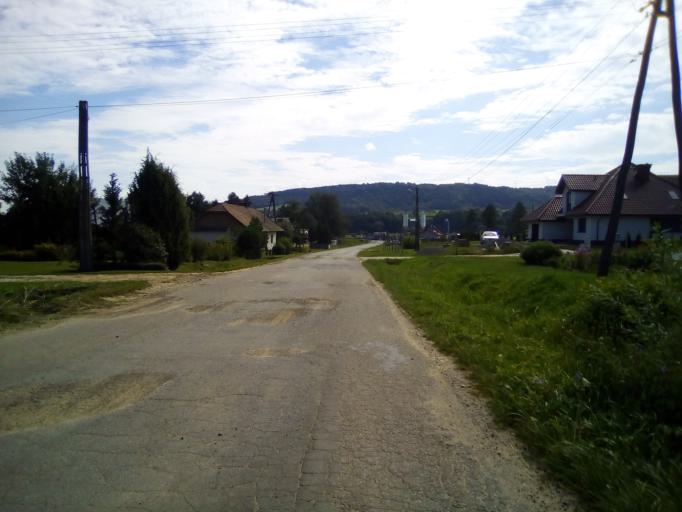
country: PL
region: Subcarpathian Voivodeship
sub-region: Powiat brzozowski
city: Domaradz
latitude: 49.8052
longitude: 21.9272
